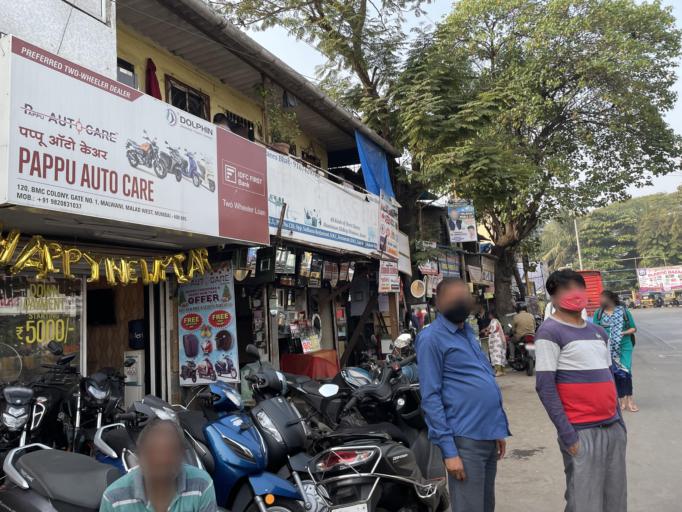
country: IN
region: Maharashtra
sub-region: Mumbai Suburban
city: Borivli
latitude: 19.1954
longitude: 72.8220
